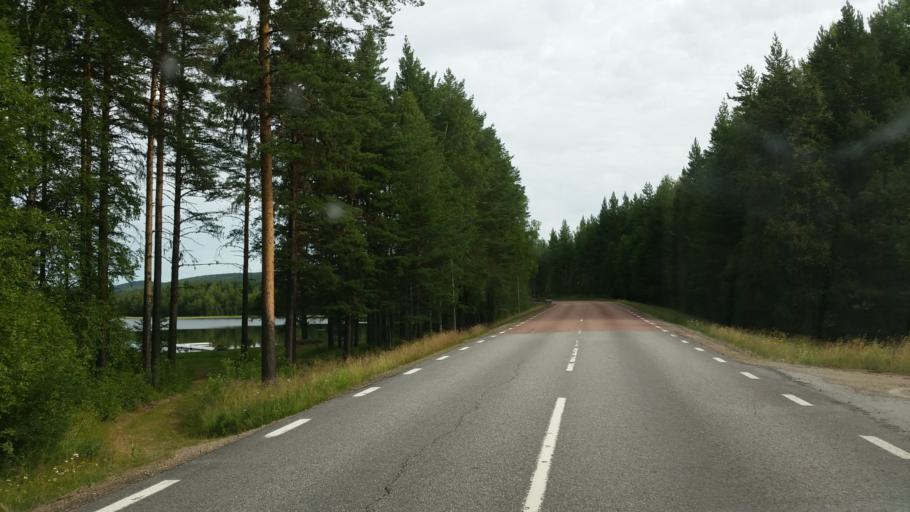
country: SE
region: Vaesternorrland
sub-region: Ange Kommun
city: Ange
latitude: 62.1907
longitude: 15.6612
